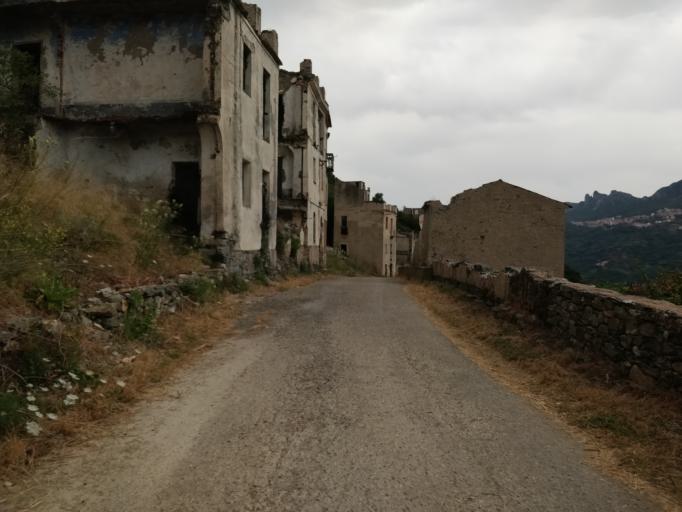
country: IT
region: Sardinia
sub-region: Provincia di Ogliastra
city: Gairo Sant'Elena
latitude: 39.8477
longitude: 9.4998
